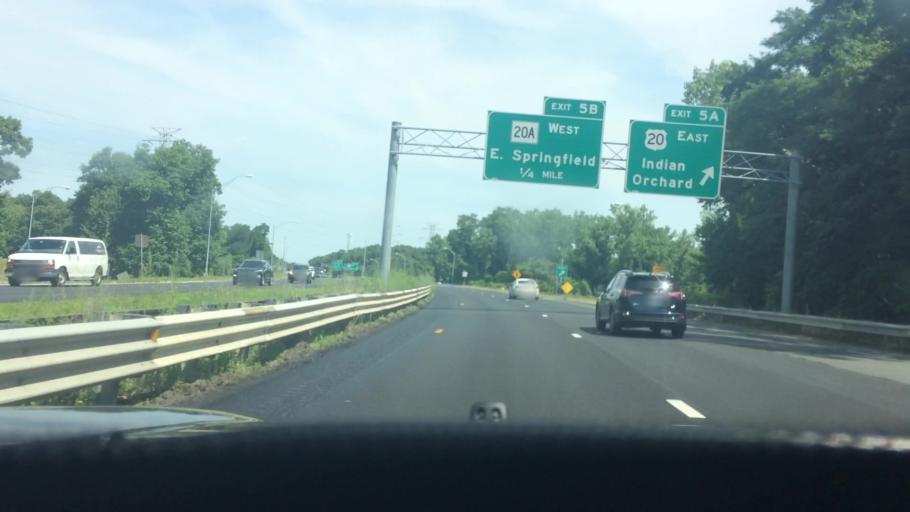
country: US
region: Massachusetts
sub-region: Hampden County
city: Springfield
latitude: 42.1432
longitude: -72.5497
